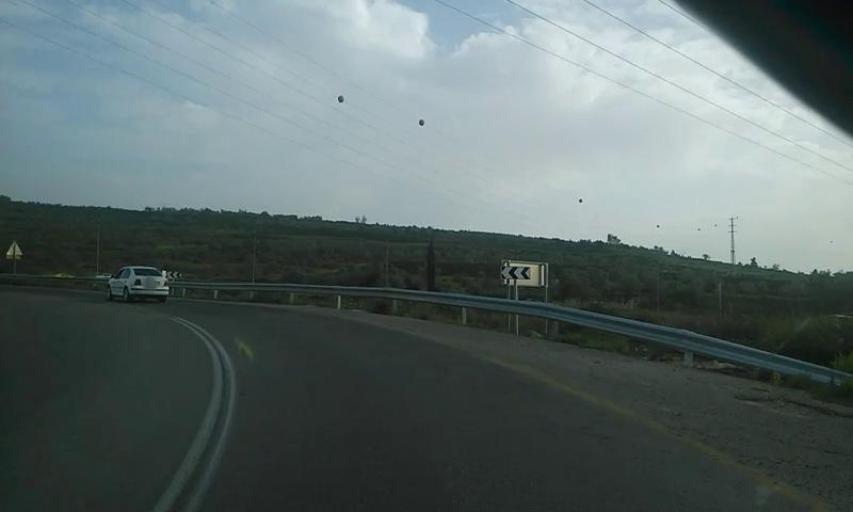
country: PS
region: West Bank
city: Immatin
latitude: 32.2038
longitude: 35.1549
